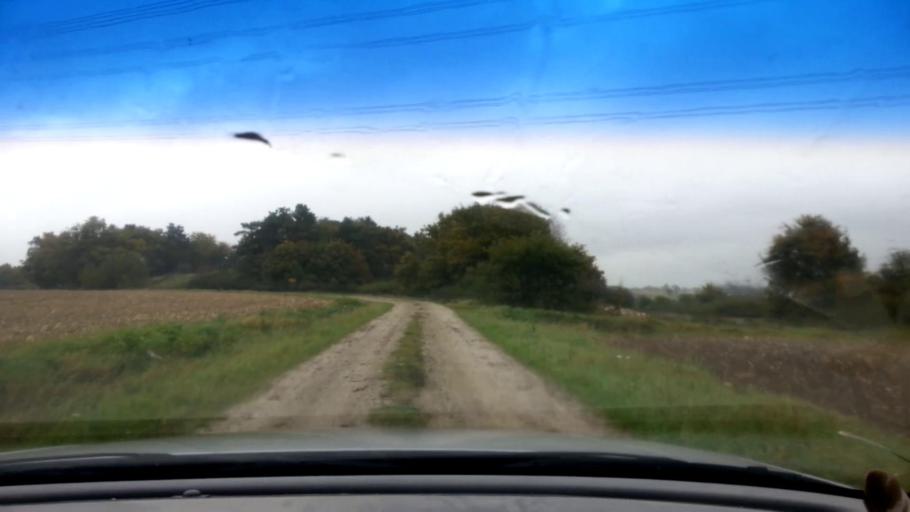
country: DE
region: Bavaria
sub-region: Upper Franconia
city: Wattendorf
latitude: 50.0356
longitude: 11.1309
